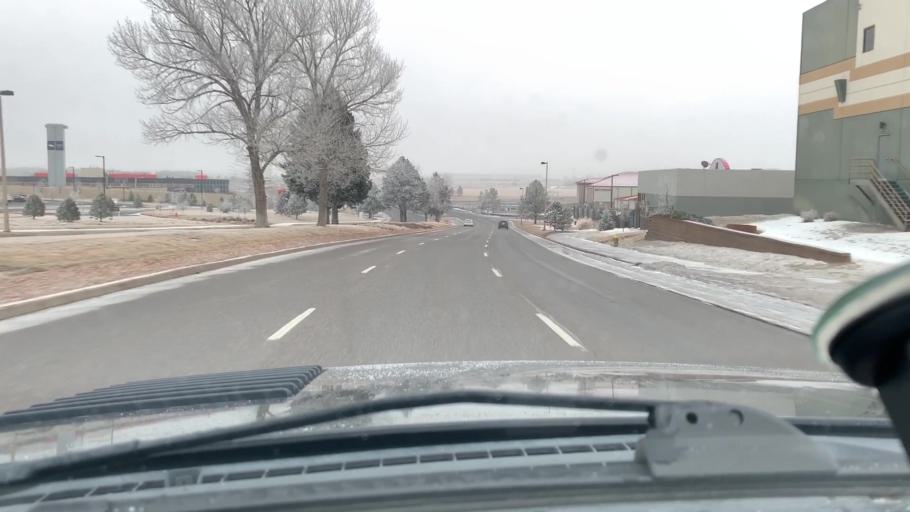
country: US
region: Colorado
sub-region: Arapahoe County
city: Dove Valley
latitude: 39.5786
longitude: -104.8350
